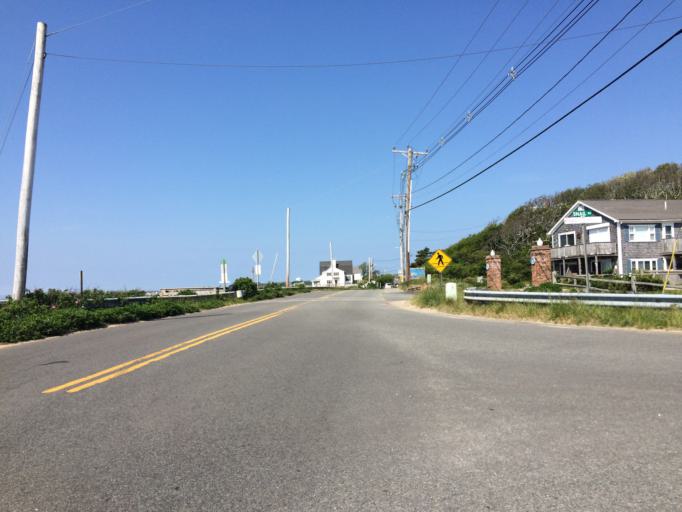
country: US
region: Massachusetts
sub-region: Barnstable County
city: Provincetown
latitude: 42.0615
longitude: -70.1625
